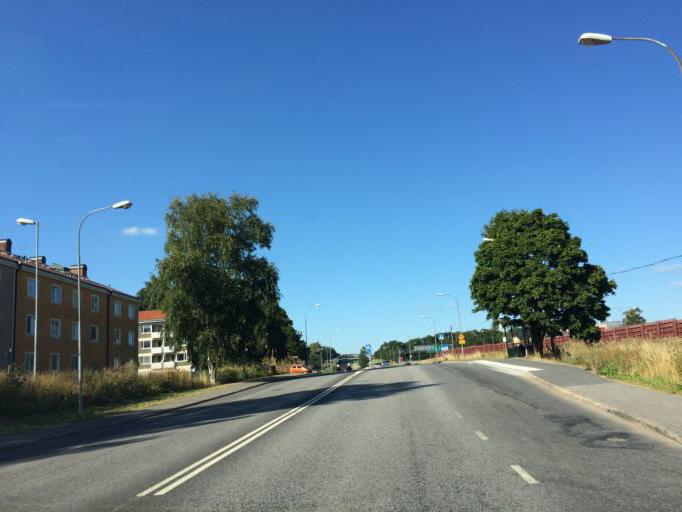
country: SE
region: Stockholm
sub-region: Upplands Vasby Kommun
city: Upplands Vaesby
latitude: 59.4808
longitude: 17.9185
